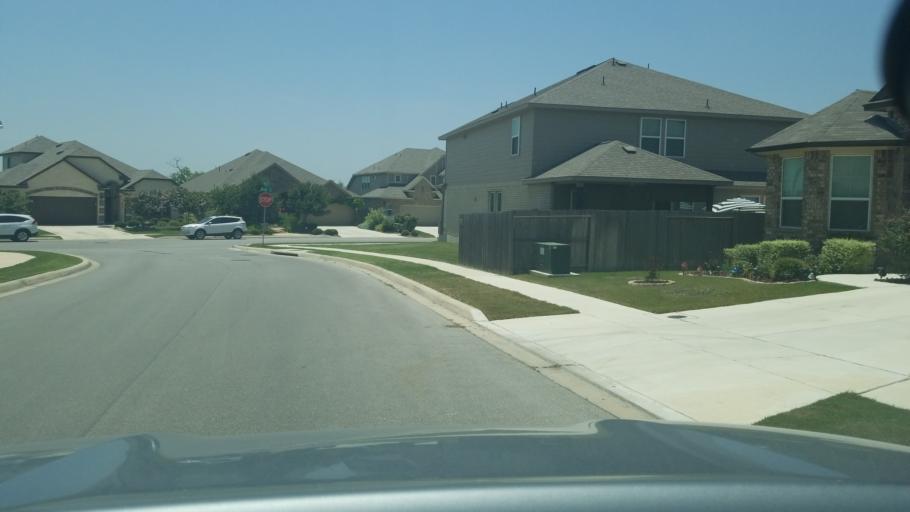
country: US
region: Texas
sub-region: Guadalupe County
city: Cibolo
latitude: 29.5800
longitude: -98.2321
